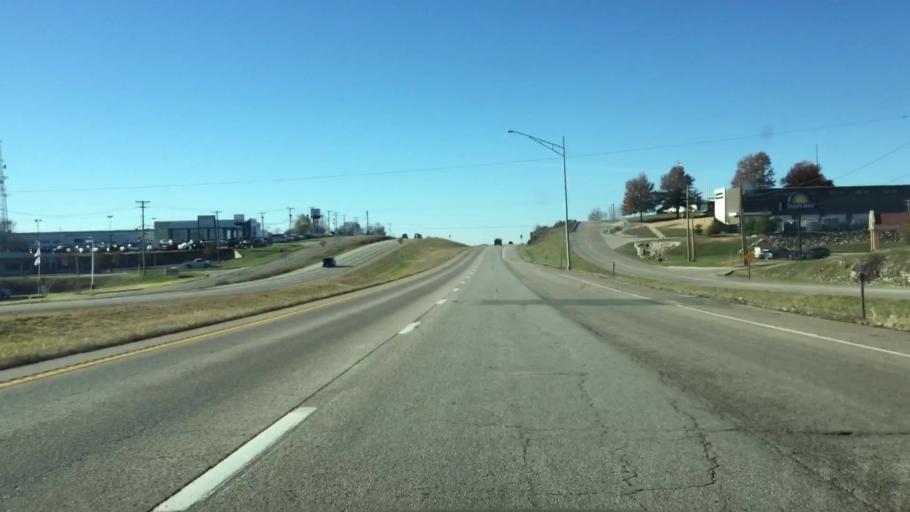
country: US
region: Missouri
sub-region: Cole County
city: Jefferson City
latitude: 38.5514
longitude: -92.2006
